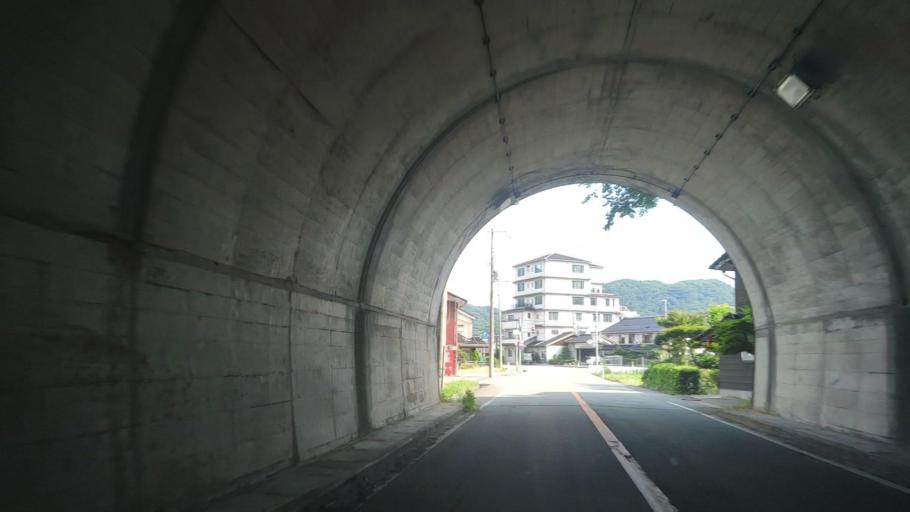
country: JP
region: Hyogo
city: Toyooka
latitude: 35.6398
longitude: 134.8359
